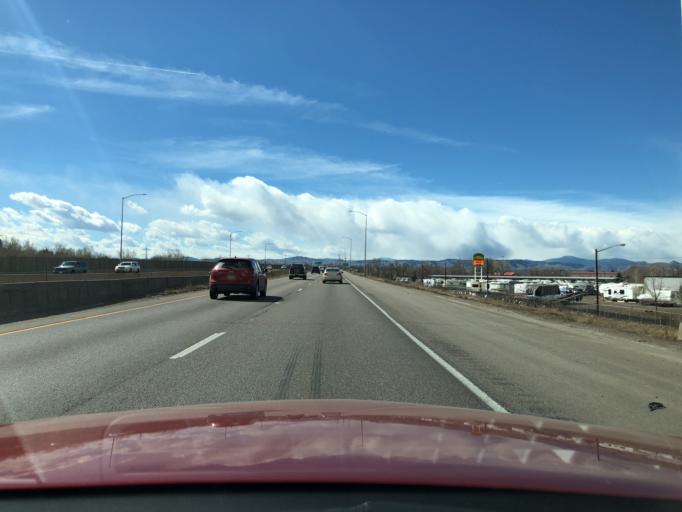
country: US
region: Colorado
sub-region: Jefferson County
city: Arvada
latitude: 39.7939
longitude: -105.0589
